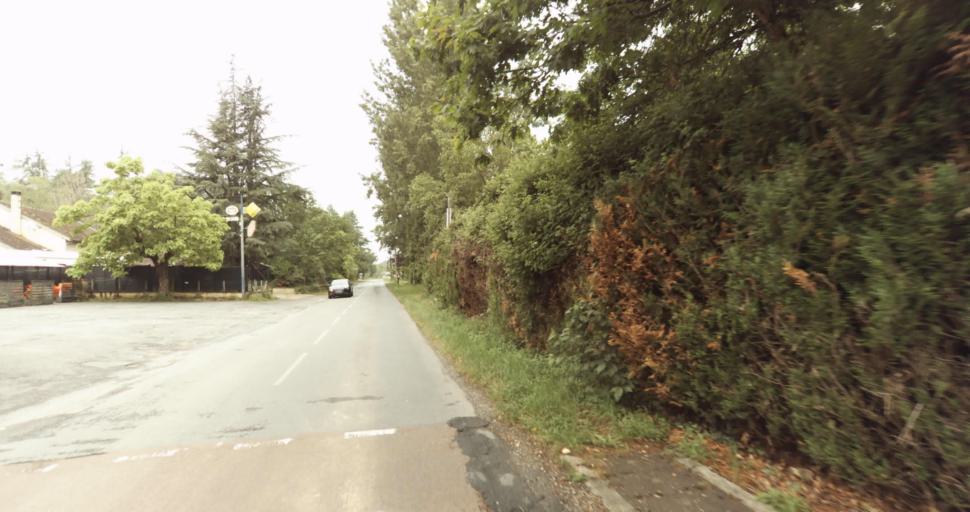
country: FR
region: Aquitaine
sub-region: Departement de la Dordogne
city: Lalinde
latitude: 44.8488
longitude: 0.7766
